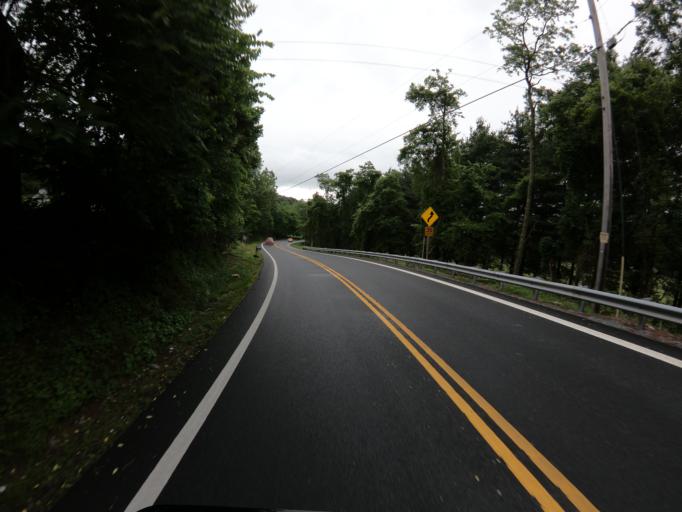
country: US
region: Maryland
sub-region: Washington County
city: Boonsboro
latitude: 39.4777
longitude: -77.6102
